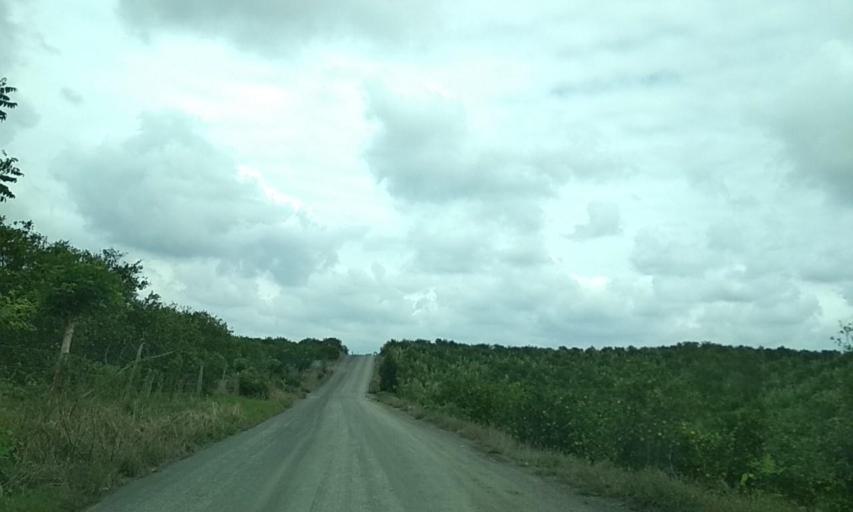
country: MX
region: Veracruz
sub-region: Papantla
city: El Chote
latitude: 20.3436
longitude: -97.3904
